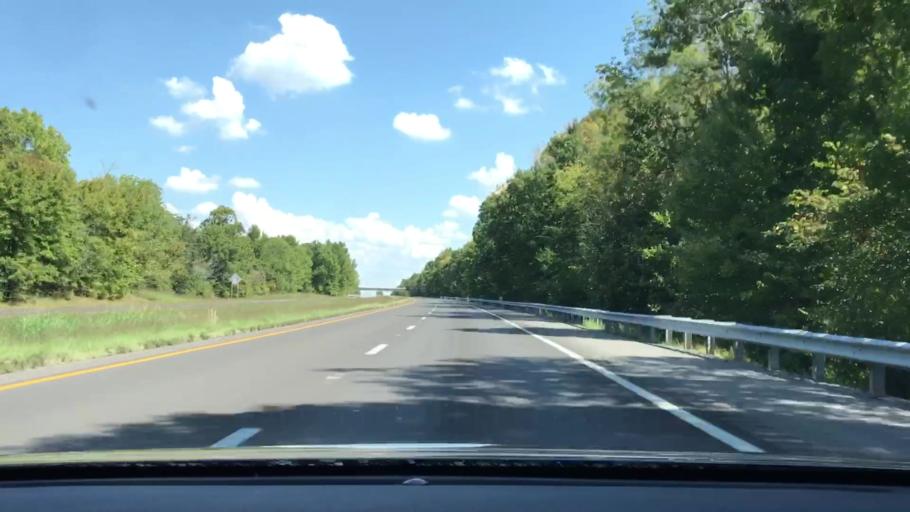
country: US
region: Kentucky
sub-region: Fulton County
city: Fulton
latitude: 36.6023
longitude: -88.7981
